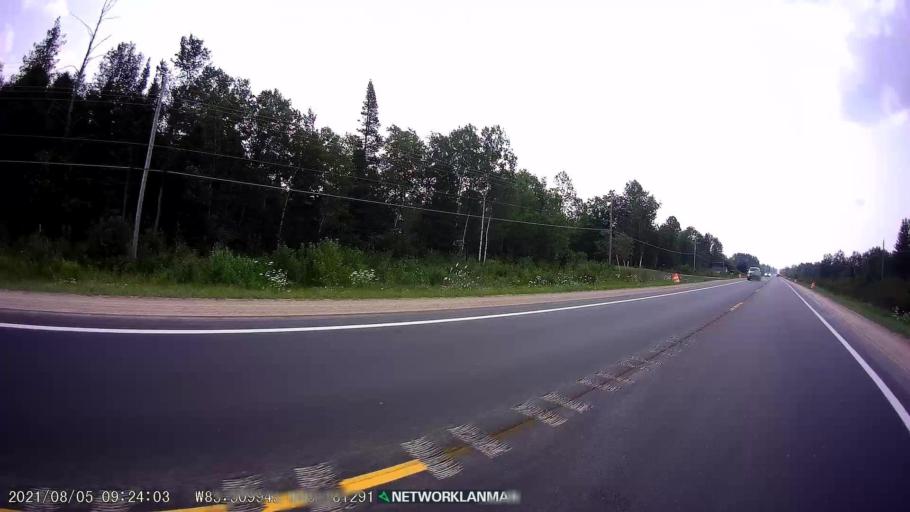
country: US
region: Michigan
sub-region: Luce County
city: Newberry
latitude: 46.3811
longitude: -85.5098
